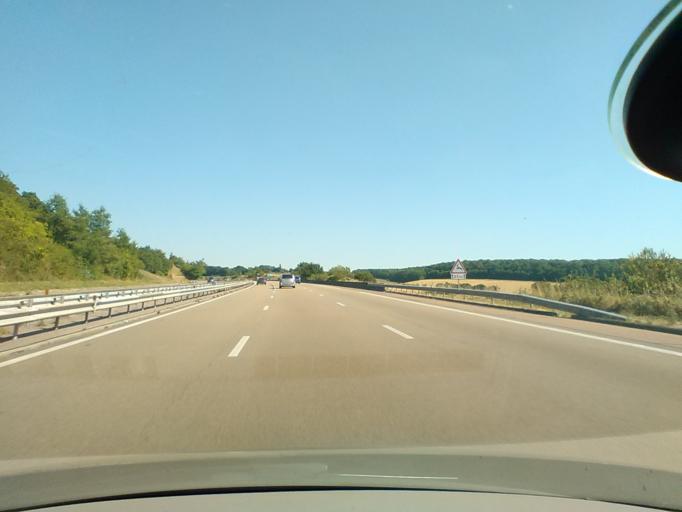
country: FR
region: Bourgogne
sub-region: Departement de l'Yonne
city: Cezy
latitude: 47.9320
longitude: 3.2509
